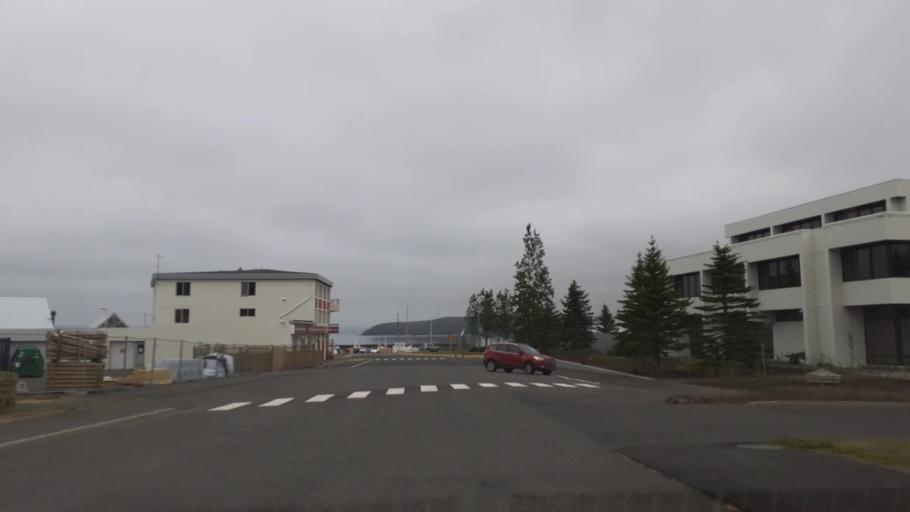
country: IS
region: Northeast
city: Dalvik
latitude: 65.9729
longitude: -18.5335
